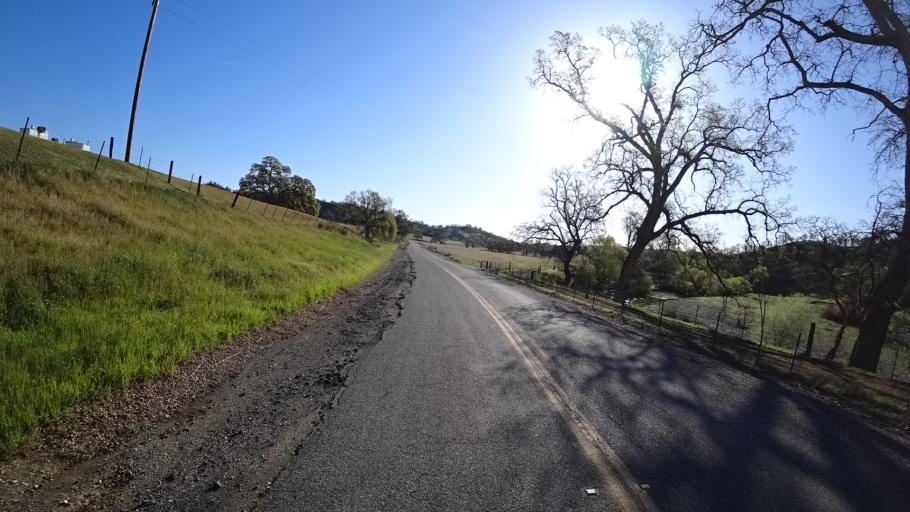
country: US
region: California
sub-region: Tehama County
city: Rancho Tehama Reserve
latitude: 39.7882
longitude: -122.4945
